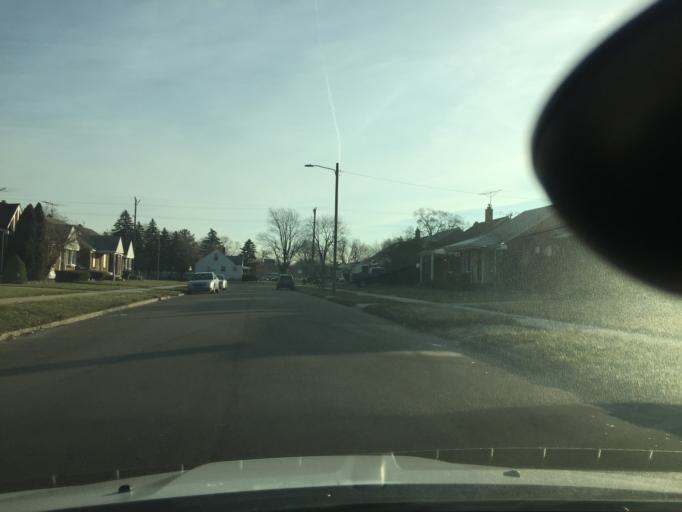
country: US
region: Michigan
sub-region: Macomb County
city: Eastpointe
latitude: 42.4418
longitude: -82.9670
